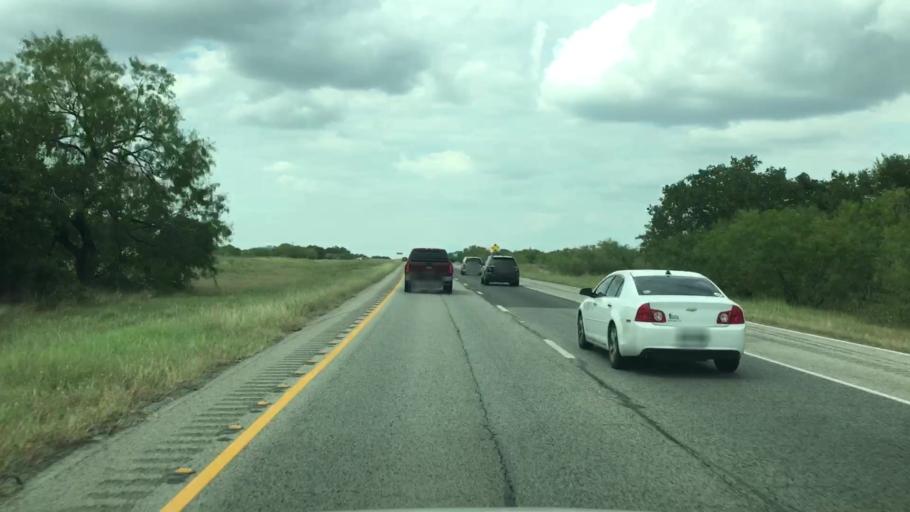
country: US
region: Texas
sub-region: Atascosa County
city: Pleasanton
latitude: 29.0433
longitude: -98.4314
